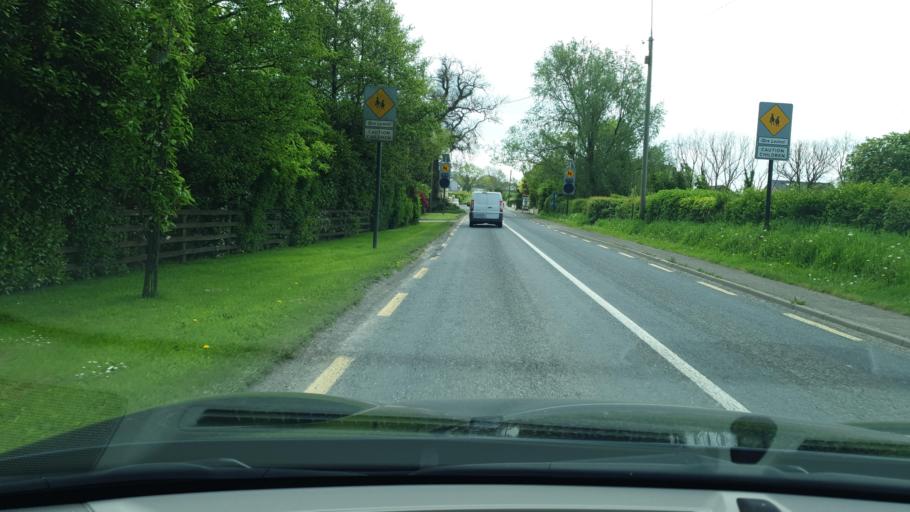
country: IE
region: Leinster
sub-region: An Mhi
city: Navan
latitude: 53.7337
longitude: -6.7107
